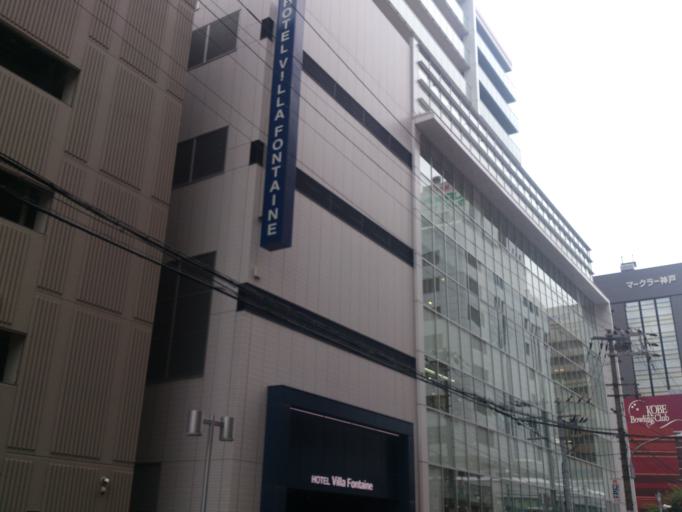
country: JP
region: Hyogo
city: Kobe
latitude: 34.6965
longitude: 135.1972
